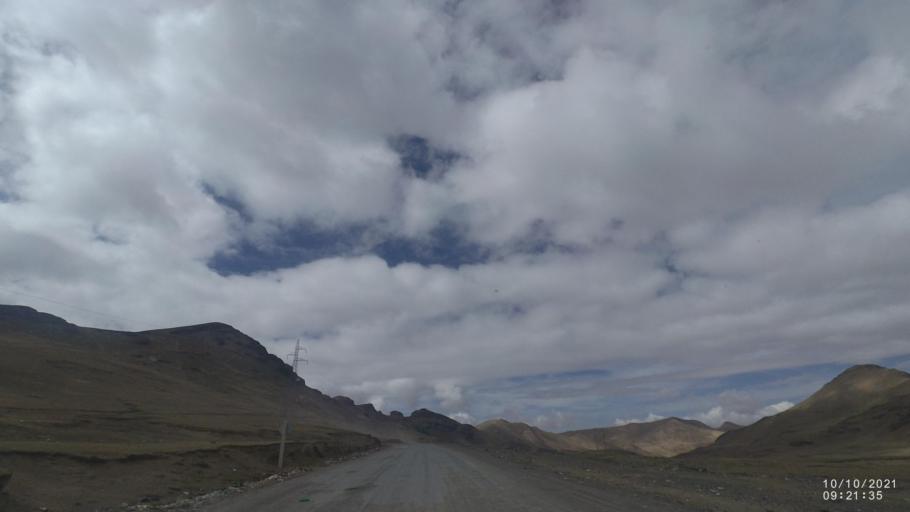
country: BO
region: La Paz
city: Quime
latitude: -17.0691
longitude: -67.2988
